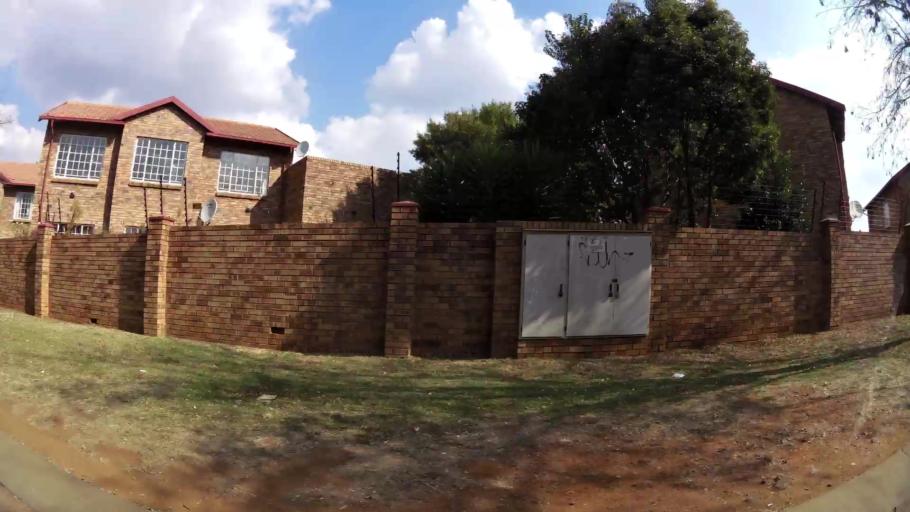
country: ZA
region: Gauteng
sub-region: City of Tshwane Metropolitan Municipality
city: Centurion
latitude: -25.8753
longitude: 28.1963
